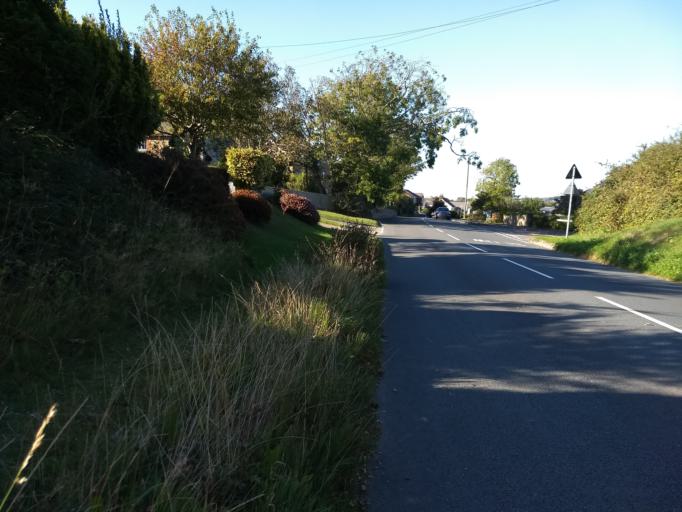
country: GB
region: England
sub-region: Isle of Wight
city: Newport
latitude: 50.6529
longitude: -1.2832
